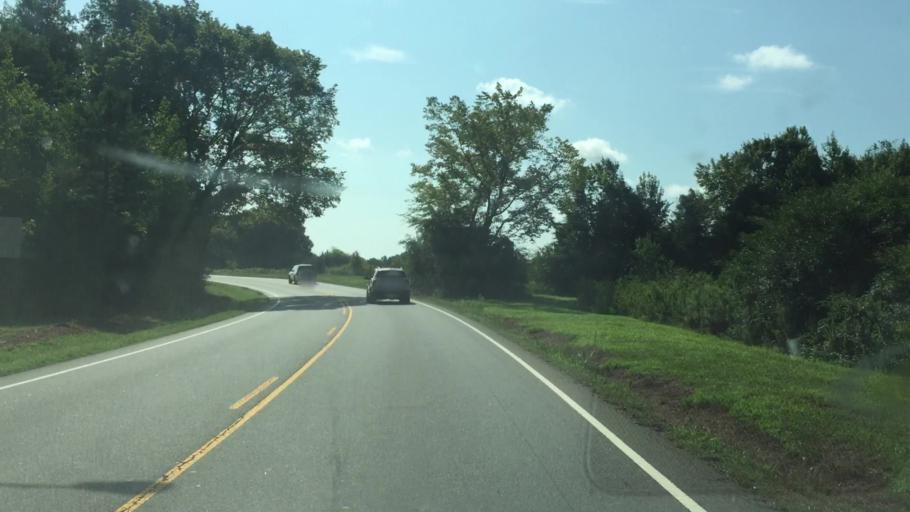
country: US
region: North Carolina
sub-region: Mecklenburg County
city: Mint Hill
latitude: 35.1728
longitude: -80.6181
